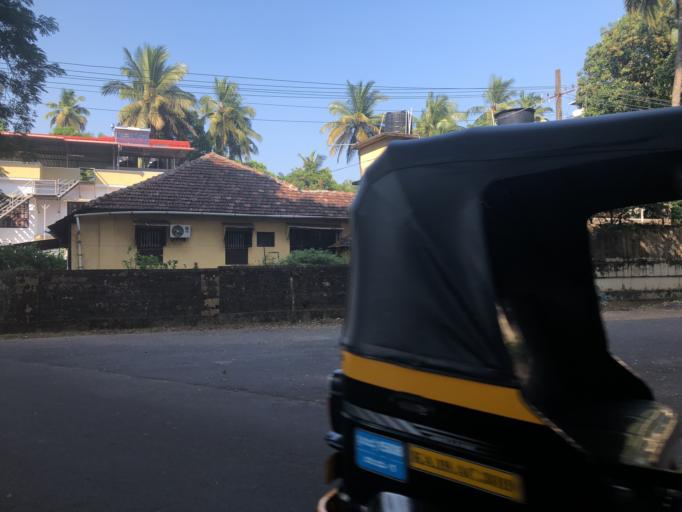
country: IN
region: Karnataka
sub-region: Dakshina Kannada
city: Mangalore
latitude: 12.8872
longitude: 74.8319
